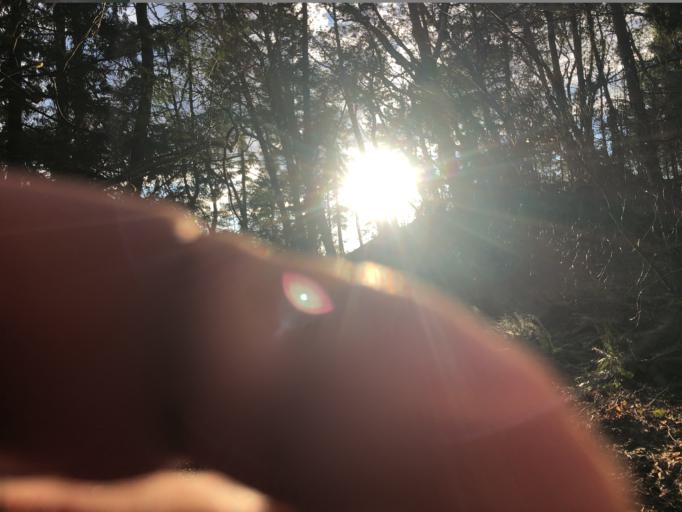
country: US
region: Washington
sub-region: Thurston County
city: Olympia
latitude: 47.0679
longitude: -122.8968
